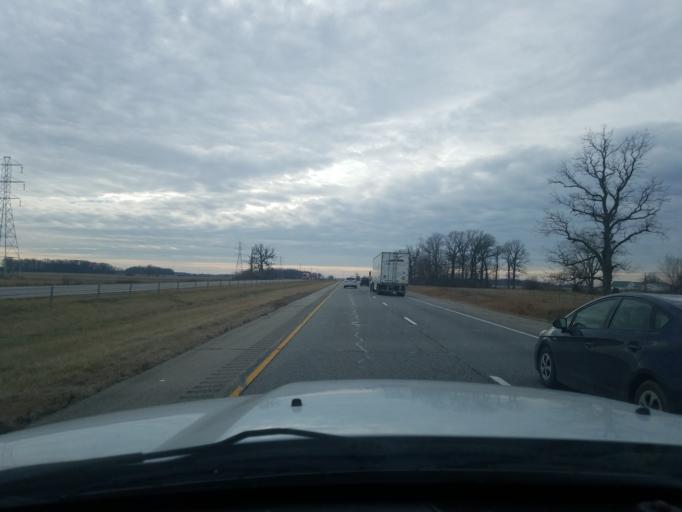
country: US
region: Indiana
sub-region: Huntington County
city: Warren
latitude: 40.6442
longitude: -85.5113
